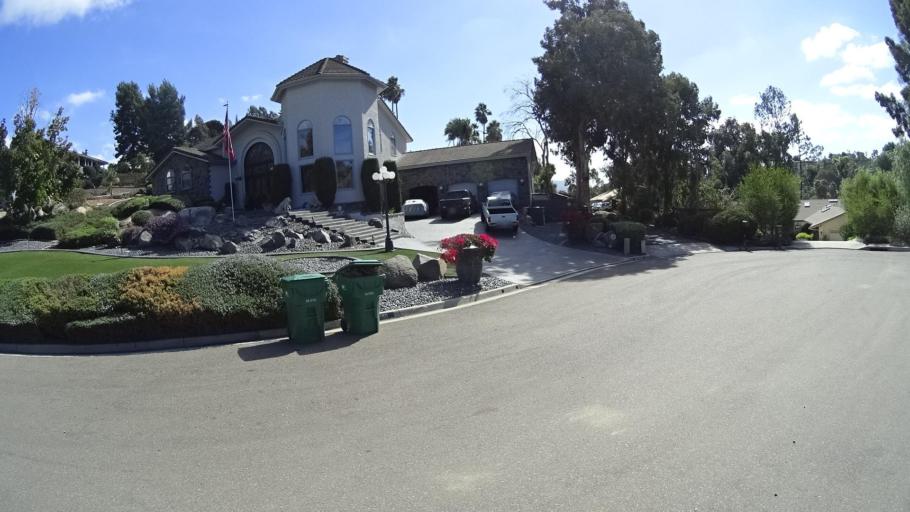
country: US
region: California
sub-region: San Diego County
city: Rancho San Diego
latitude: 32.7669
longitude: -116.9353
